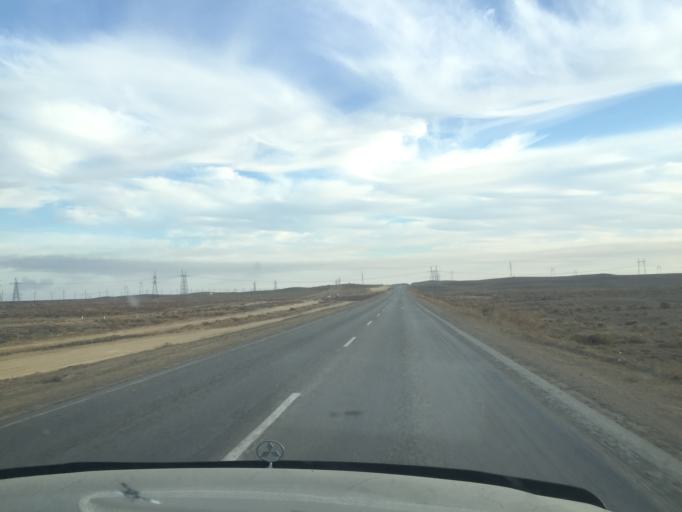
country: KZ
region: Almaty Oblysy
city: Ulken
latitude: 45.1502
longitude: 73.9531
